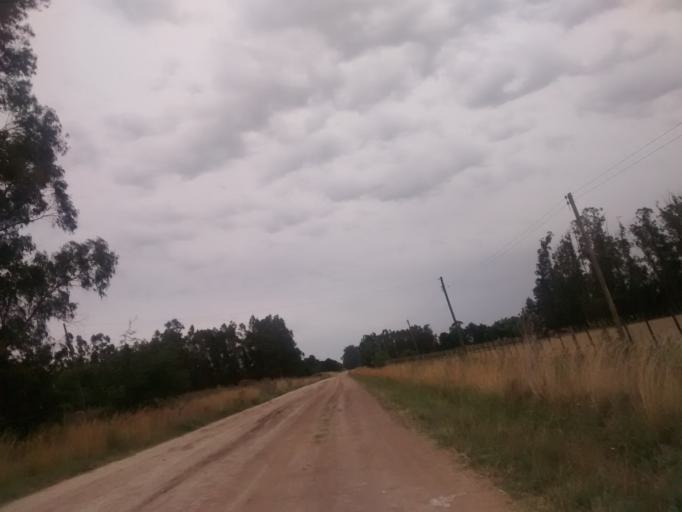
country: AR
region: Buenos Aires
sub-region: Partido de Loberia
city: Loberia
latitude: -38.1926
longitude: -58.7388
